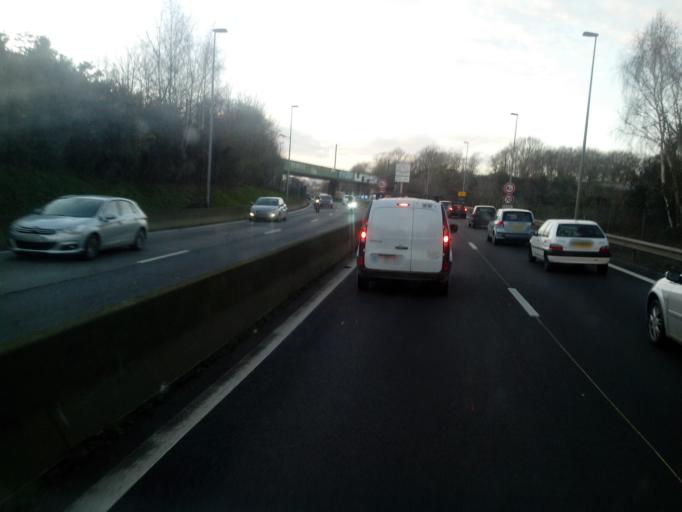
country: FR
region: Pays de la Loire
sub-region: Departement de la Loire-Atlantique
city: Nantes
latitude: 47.2564
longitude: -1.5402
